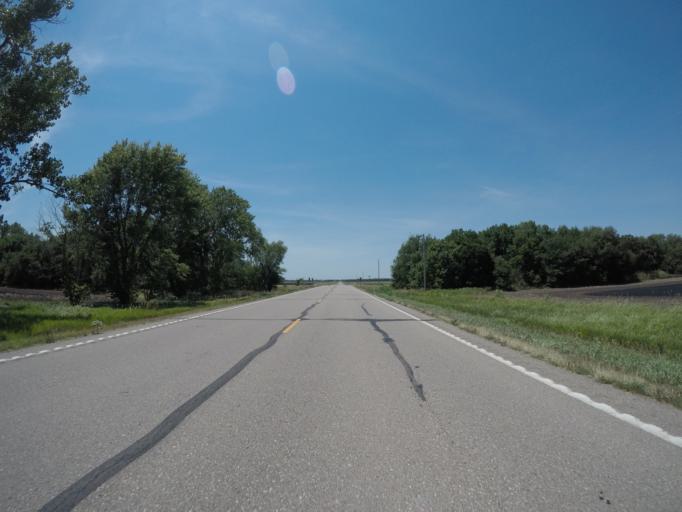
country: US
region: Kansas
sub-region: Ottawa County
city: Minneapolis
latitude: 39.0306
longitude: -97.5557
